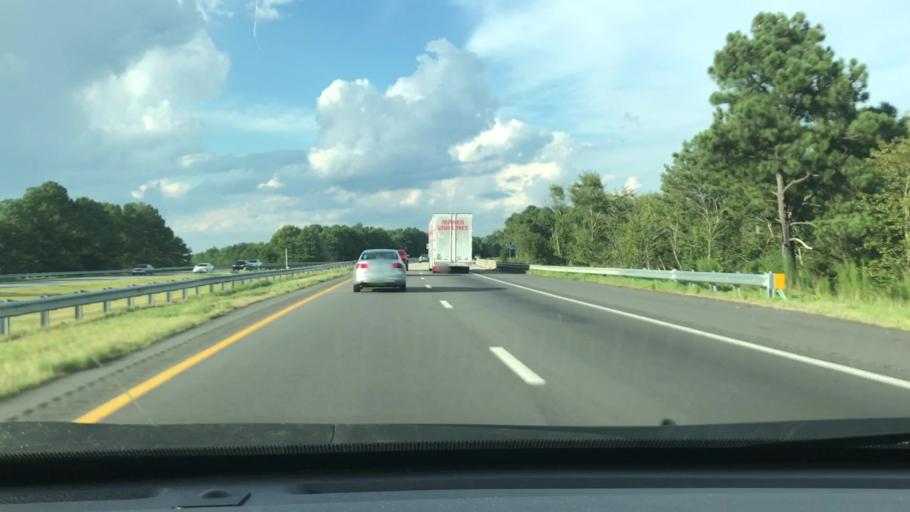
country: US
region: North Carolina
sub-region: Cumberland County
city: Hope Mills
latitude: 34.9299
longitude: -78.9393
